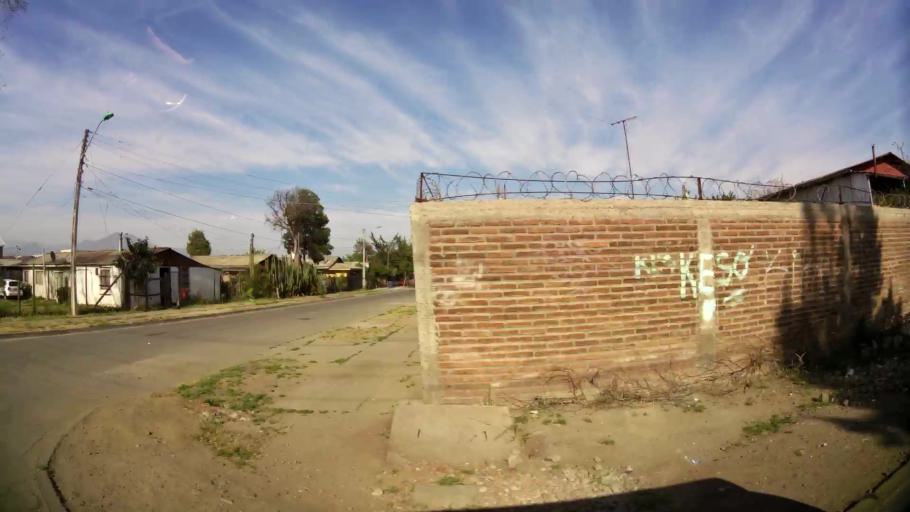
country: CL
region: Santiago Metropolitan
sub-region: Provincia de Talagante
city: Talagante
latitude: -33.6758
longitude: -70.9440
